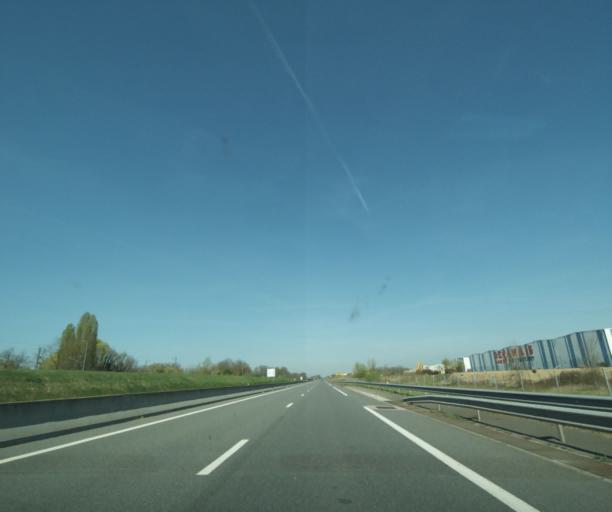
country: FR
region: Auvergne
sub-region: Departement de l'Allier
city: Avermes
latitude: 46.6068
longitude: 3.2963
